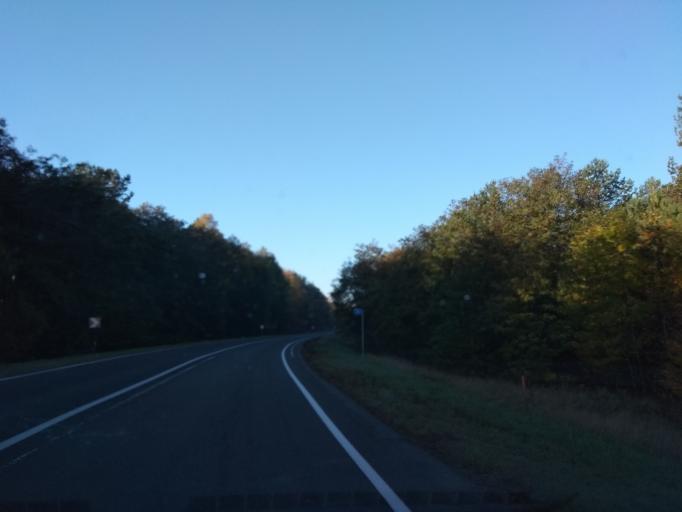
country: BY
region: Brest
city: Kobryn
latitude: 52.0133
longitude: 24.2320
